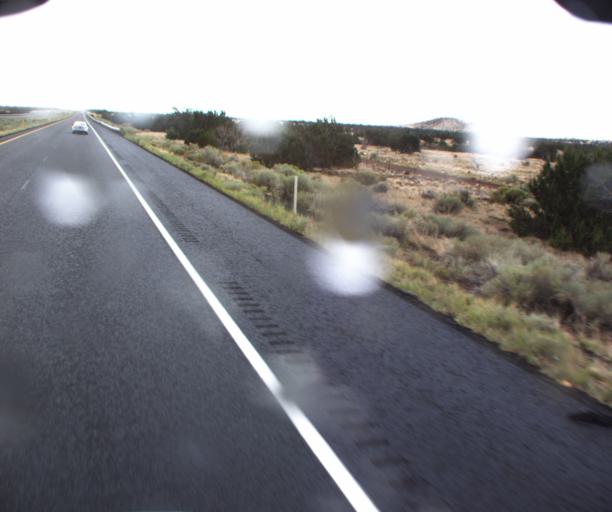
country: US
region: Arizona
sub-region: Coconino County
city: Flagstaff
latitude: 35.1710
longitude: -111.3306
